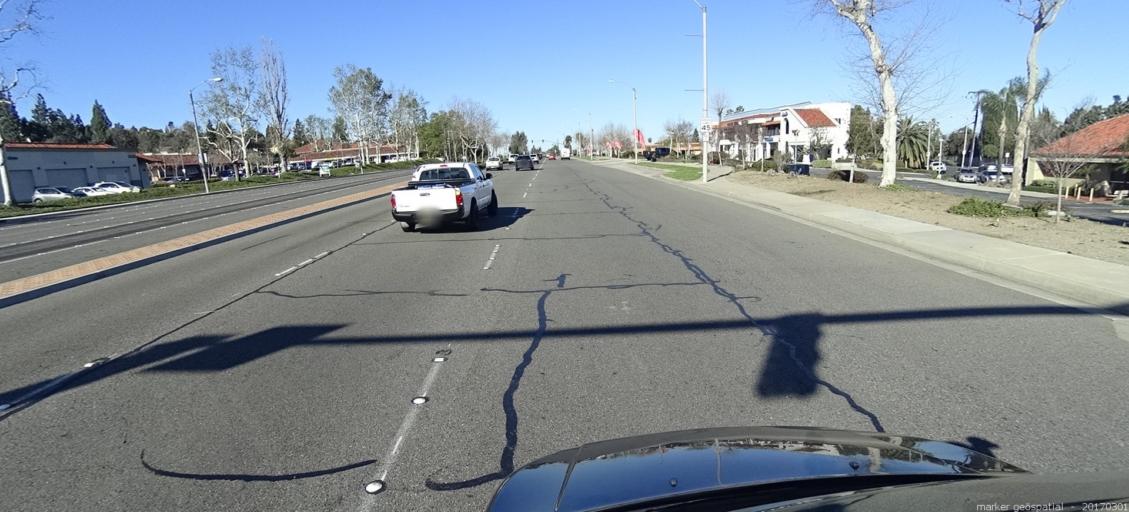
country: US
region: California
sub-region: Orange County
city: Villa Park
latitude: 33.8514
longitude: -117.7909
